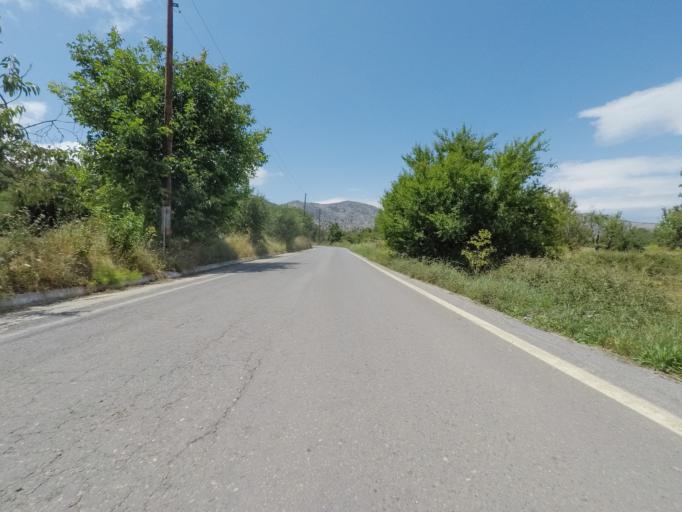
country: GR
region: Crete
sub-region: Nomos Irakleiou
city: Mokhos
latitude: 35.1675
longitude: 25.4486
